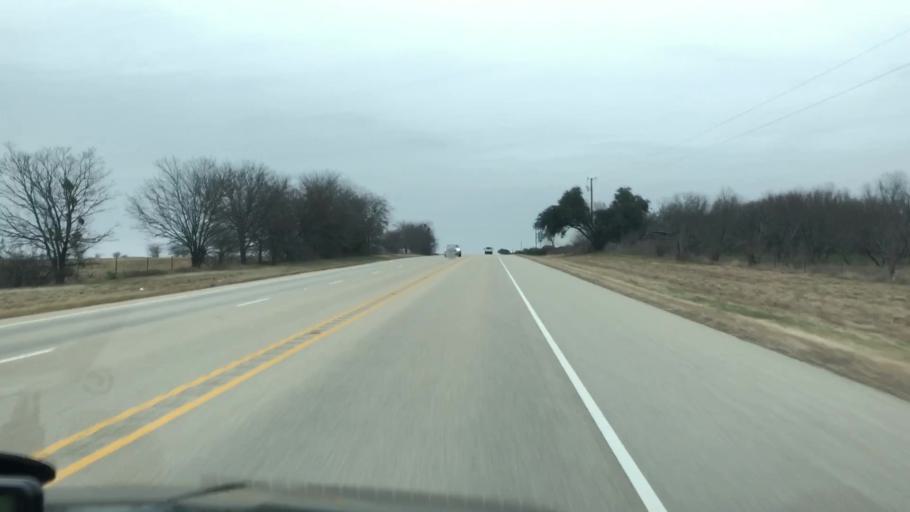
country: US
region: Texas
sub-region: Hamilton County
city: Hamilton
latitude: 31.5674
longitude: -98.1585
